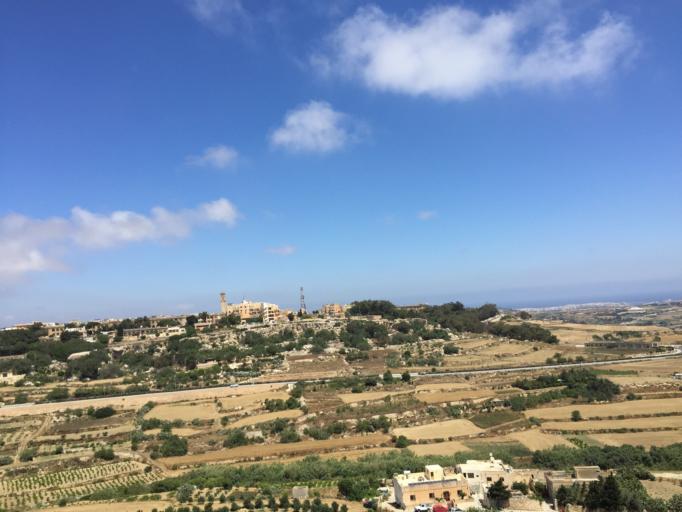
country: MT
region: L-Imdina
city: Imdina
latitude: 35.8877
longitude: 14.4028
